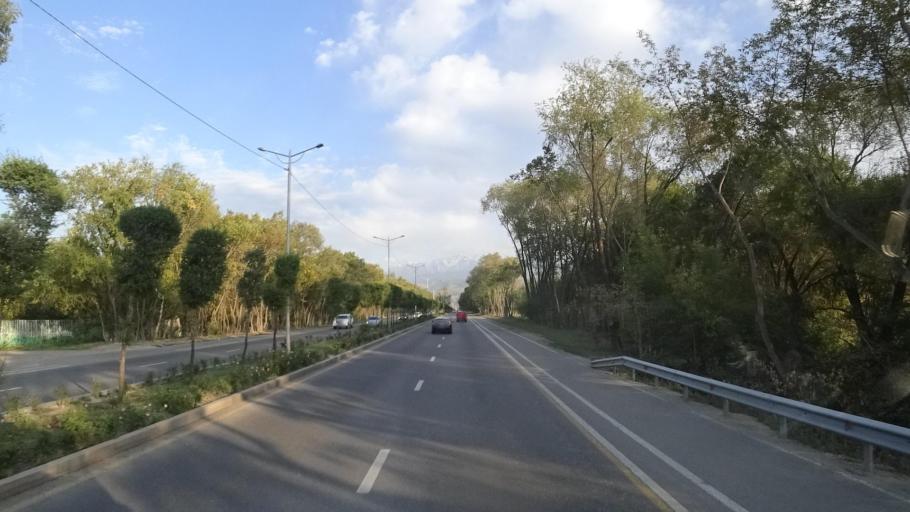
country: KZ
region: Almaty Oblysy
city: Pervomayskiy
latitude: 43.3273
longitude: 77.0138
